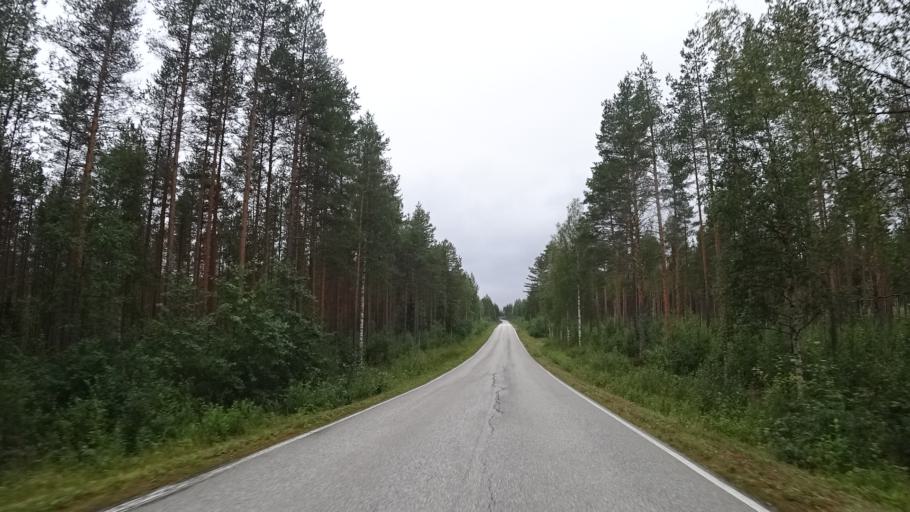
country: FI
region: North Karelia
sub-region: Pielisen Karjala
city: Lieksa
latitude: 63.3727
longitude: 30.3013
